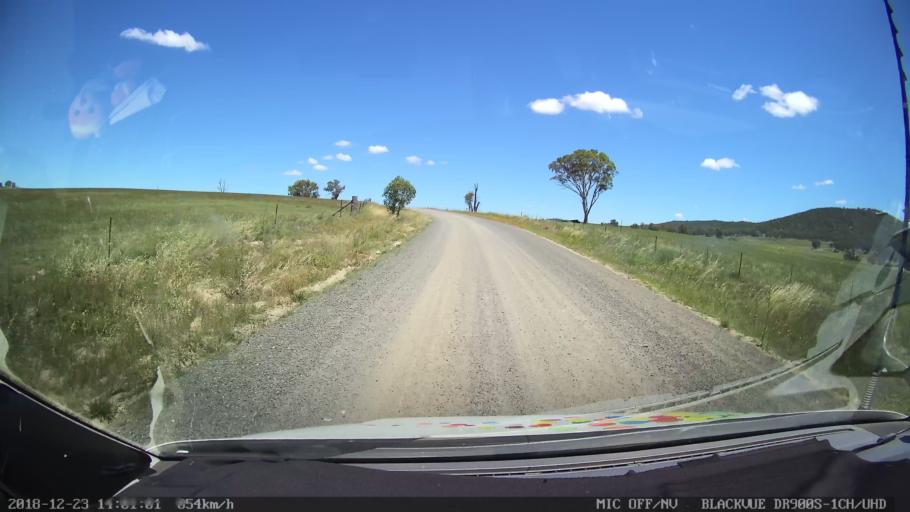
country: AU
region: New South Wales
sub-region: Tamworth Municipality
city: Manilla
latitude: -30.6183
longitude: 151.1087
